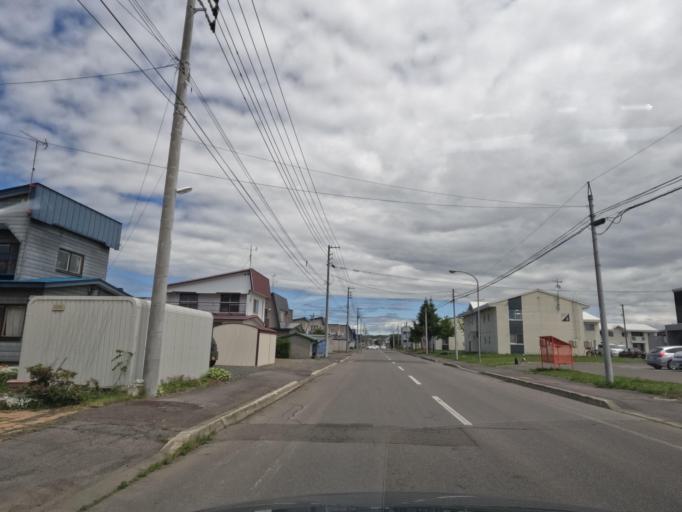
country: JP
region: Hokkaido
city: Shimo-furano
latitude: 43.4550
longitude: 142.4624
